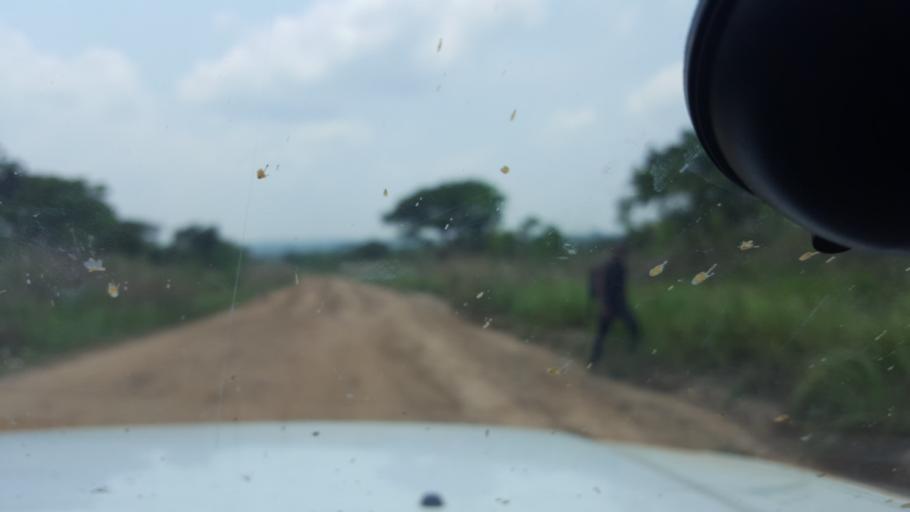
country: CD
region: Bandundu
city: Mushie
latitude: -3.7516
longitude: 16.6412
